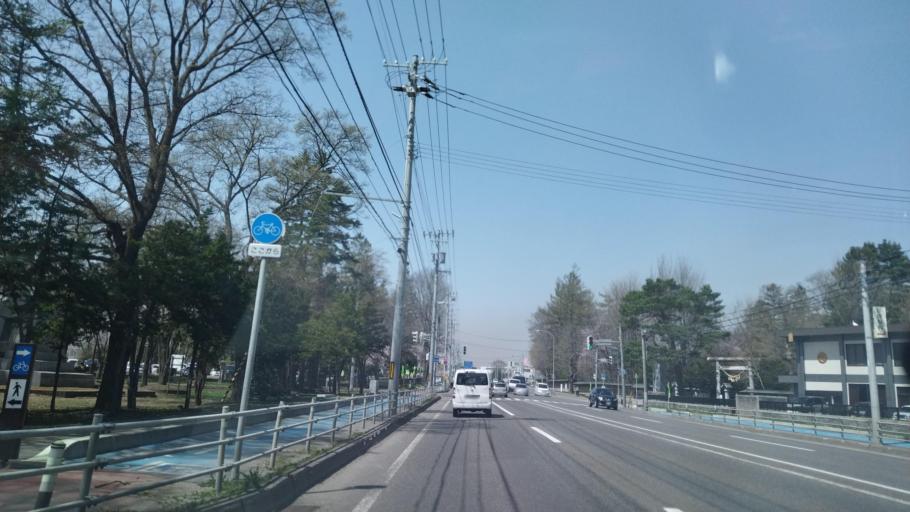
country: JP
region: Hokkaido
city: Obihiro
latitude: 42.9303
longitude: 143.2100
